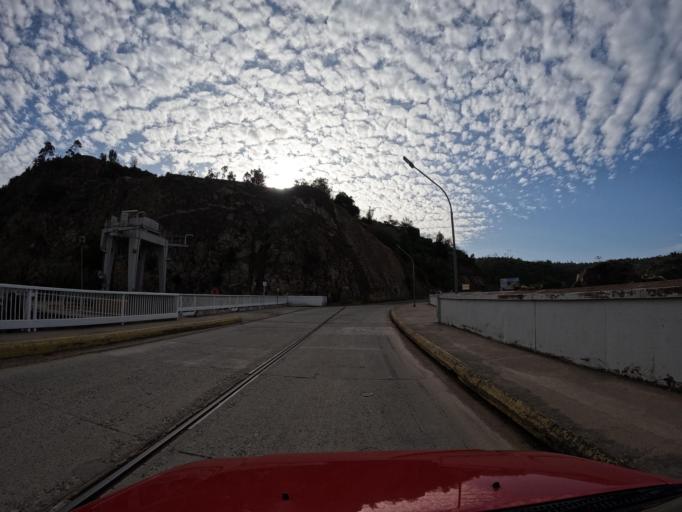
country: CL
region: Valparaiso
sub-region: San Antonio Province
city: San Antonio
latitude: -34.0416
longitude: -71.5900
